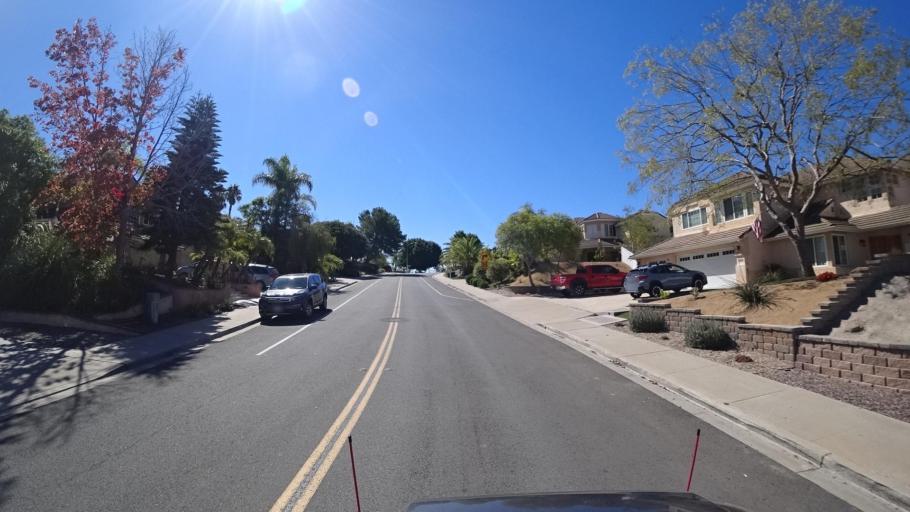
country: US
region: California
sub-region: San Diego County
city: Bonita
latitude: 32.6544
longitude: -116.9859
